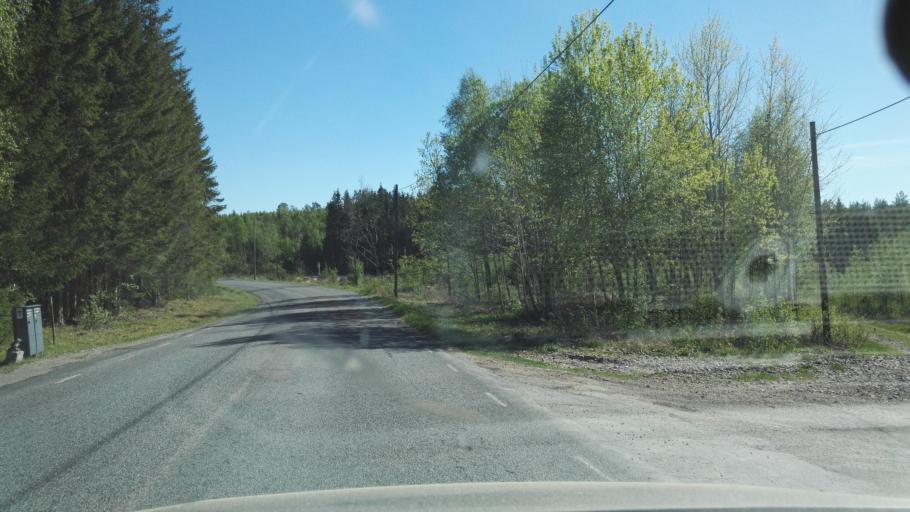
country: SE
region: Kronoberg
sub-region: Vaxjo Kommun
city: Rottne
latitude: 57.0788
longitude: 14.8197
